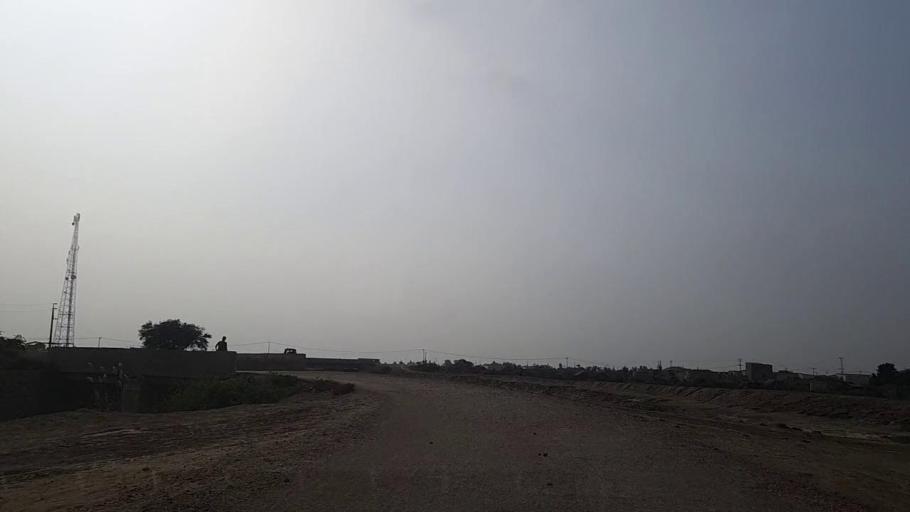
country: PK
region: Sindh
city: Mirpur Sakro
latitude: 24.6381
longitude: 67.5936
